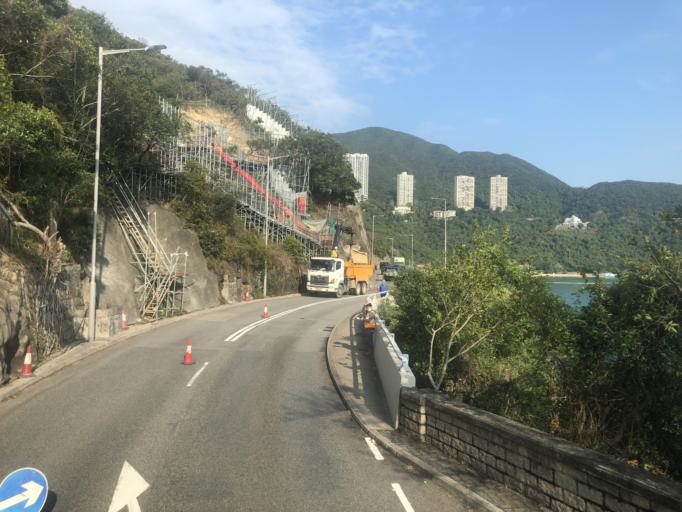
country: HK
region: Wanchai
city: Wan Chai
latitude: 22.2453
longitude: 114.1807
